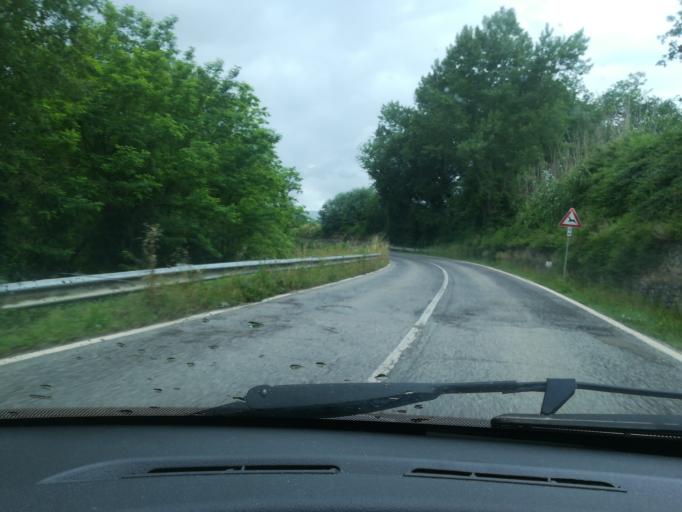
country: IT
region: The Marches
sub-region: Provincia di Macerata
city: San Ginesio
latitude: 43.0978
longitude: 13.3350
